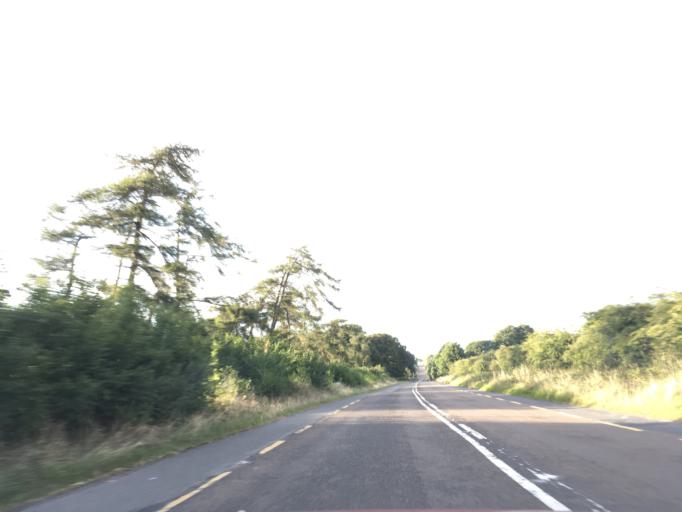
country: IE
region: Munster
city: Cashel
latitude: 52.4798
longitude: -7.8922
